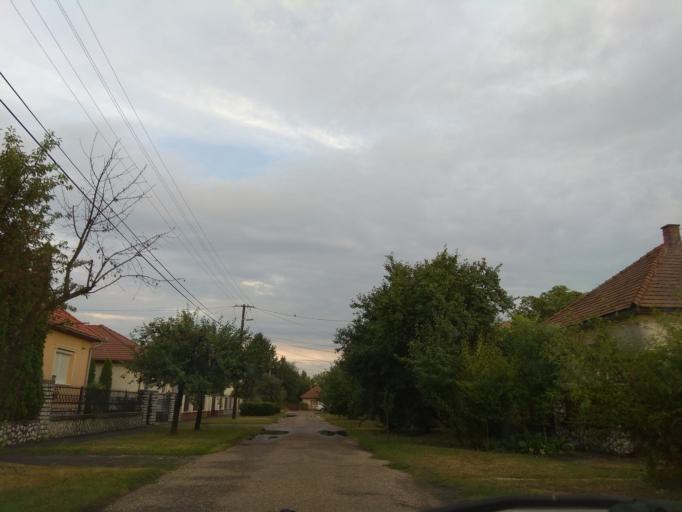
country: HU
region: Borsod-Abauj-Zemplen
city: Miskolc
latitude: 48.0742
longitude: 20.8213
